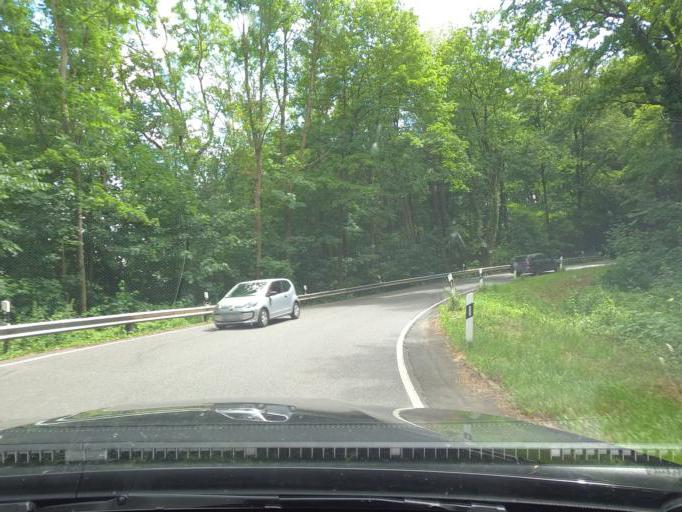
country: DE
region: Lower Saxony
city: Elbe
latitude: 52.1214
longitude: 10.2973
